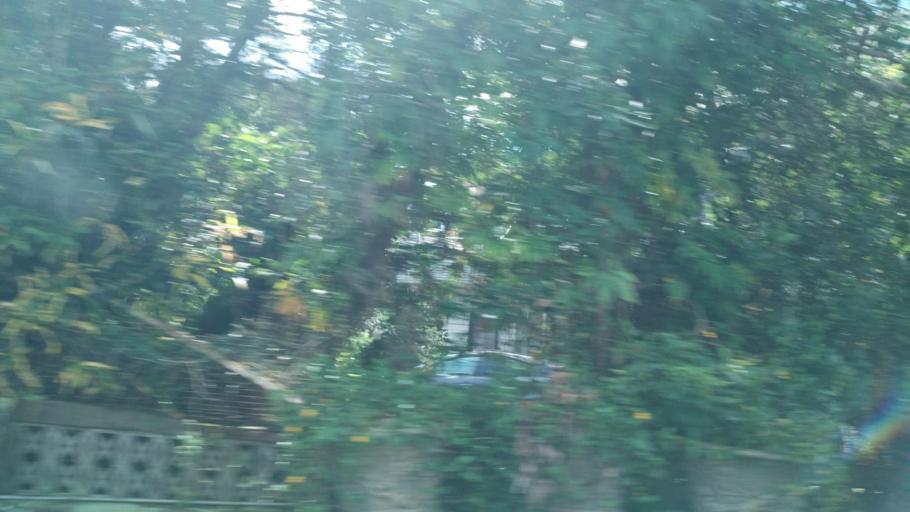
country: TW
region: Taipei
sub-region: Taipei
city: Banqiao
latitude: 24.9488
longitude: 121.5051
